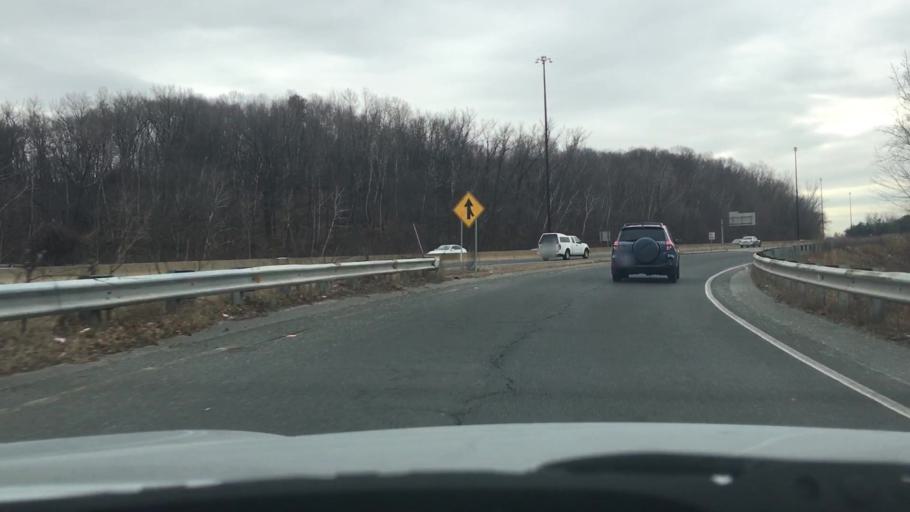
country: US
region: Massachusetts
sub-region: Hampden County
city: North Chicopee
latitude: 42.1791
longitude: -72.6073
